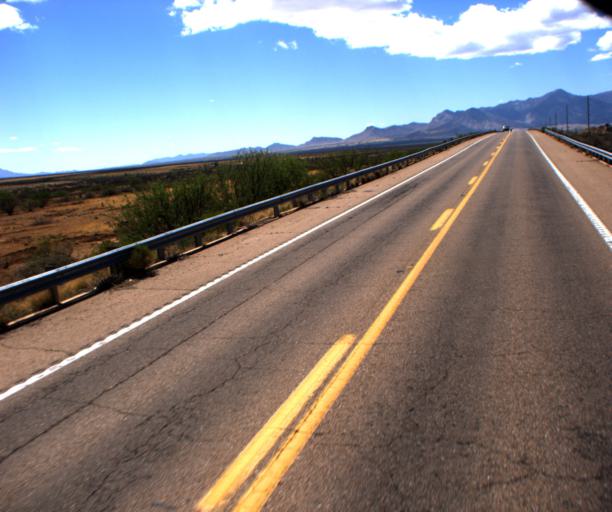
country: US
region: Arizona
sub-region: Cochise County
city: Naco
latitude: 31.3800
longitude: -110.0450
